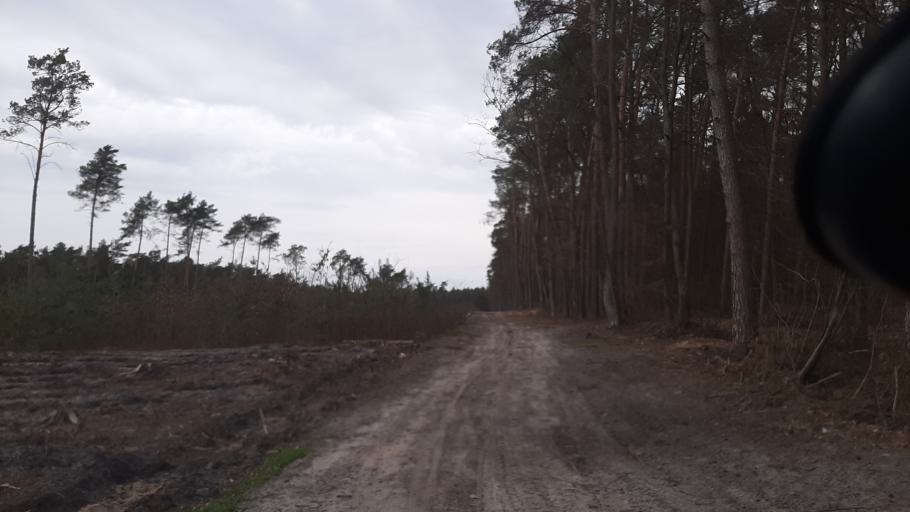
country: PL
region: Lublin Voivodeship
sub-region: Powiat lubelski
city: Garbow
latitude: 51.3951
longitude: 22.3782
